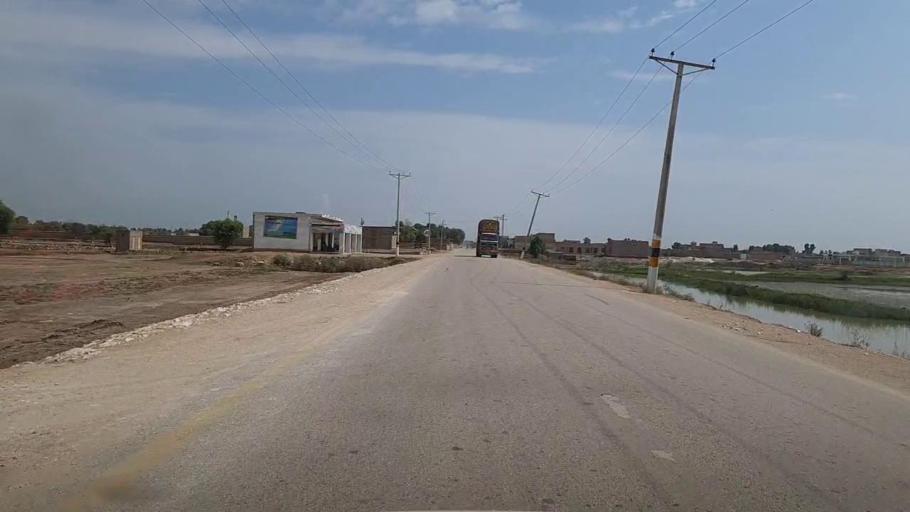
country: PK
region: Sindh
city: Thul
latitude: 28.2491
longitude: 68.7832
